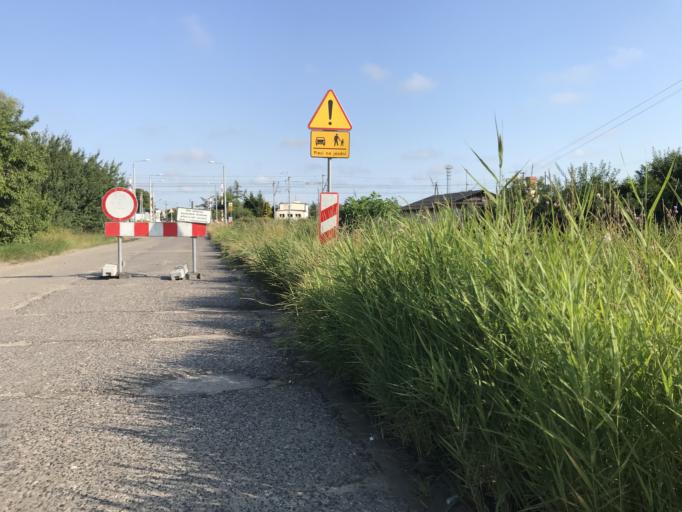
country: PL
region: Pomeranian Voivodeship
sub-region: Gdansk
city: Gdansk
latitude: 54.3397
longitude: 18.6870
